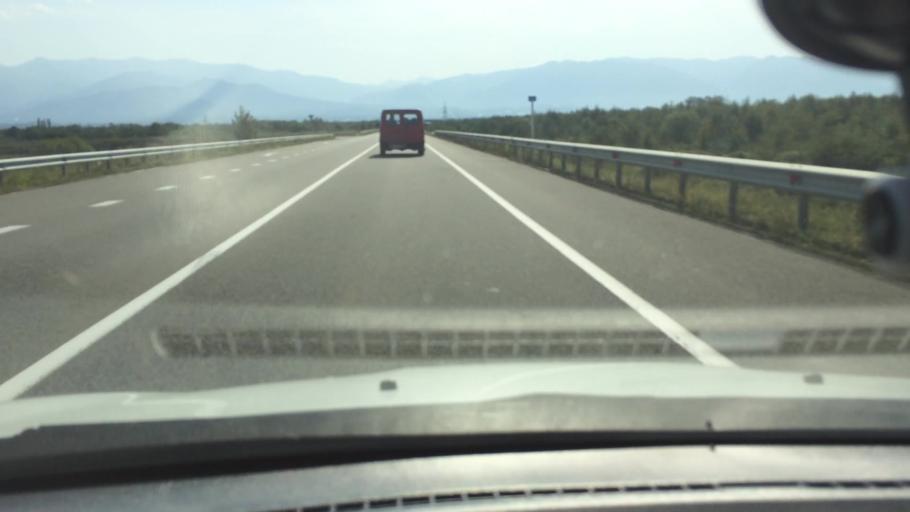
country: GE
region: Ajaria
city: Ochkhamuri
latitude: 41.8979
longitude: 41.7981
